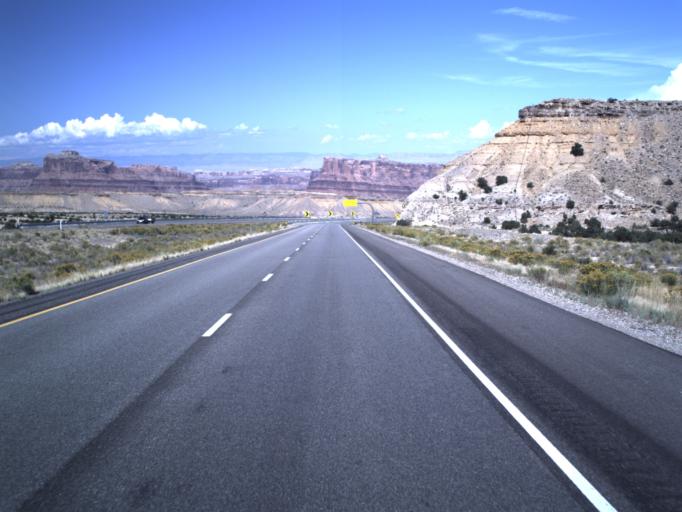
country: US
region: Utah
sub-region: Emery County
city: Castle Dale
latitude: 38.9260
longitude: -110.4966
